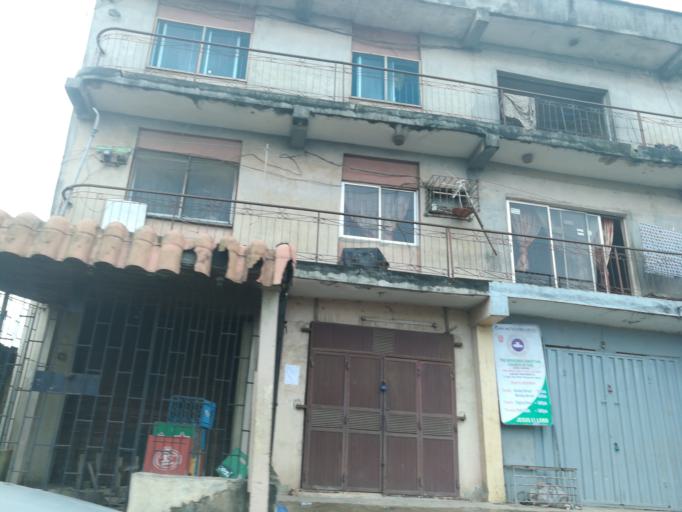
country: NG
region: Lagos
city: Oshodi
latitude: 6.5761
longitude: 3.3425
